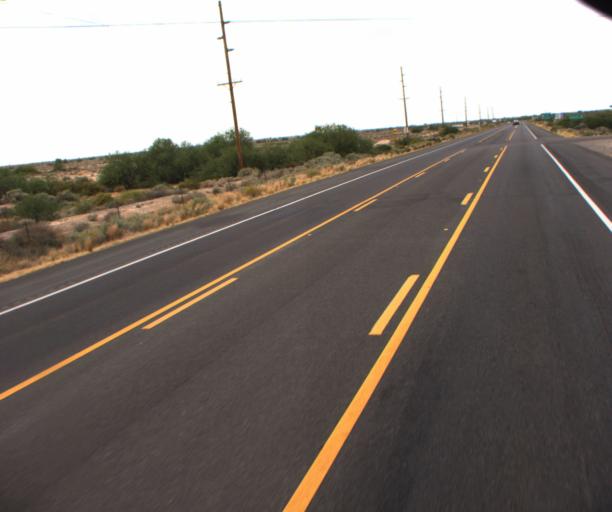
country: US
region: Arizona
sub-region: Pinal County
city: Sacaton
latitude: 33.0592
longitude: -111.6860
